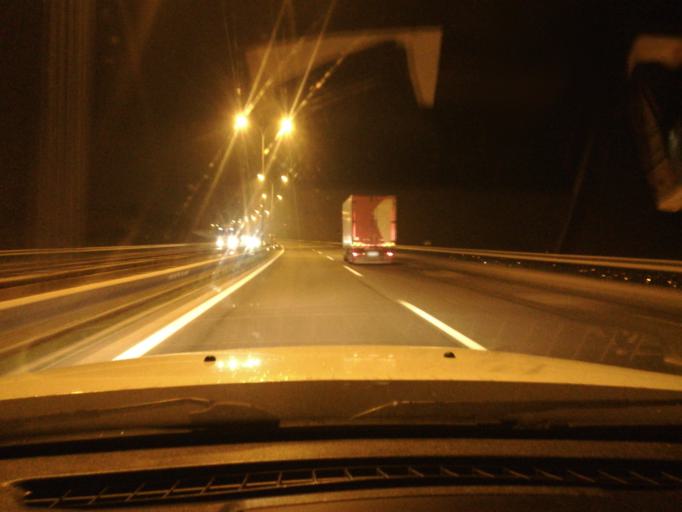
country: TR
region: Istanbul
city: Celaliye
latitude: 41.0507
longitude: 28.4397
